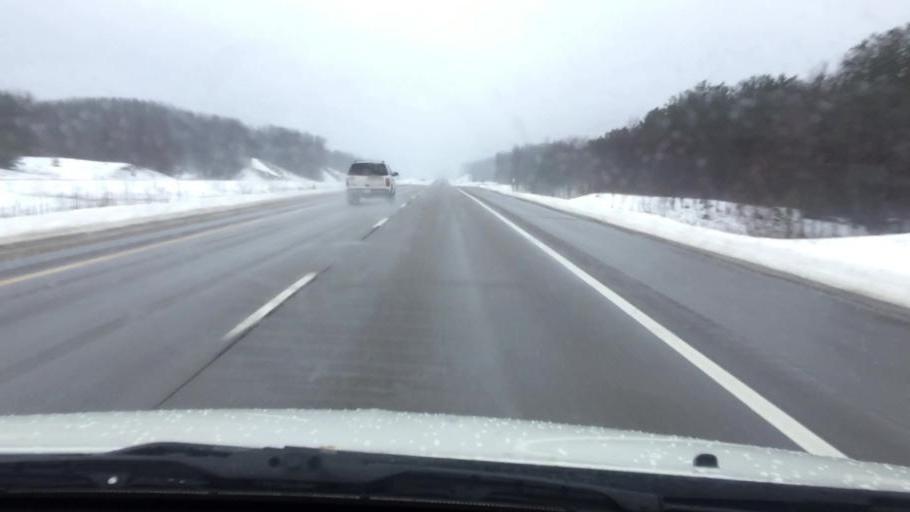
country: US
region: Michigan
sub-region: Wexford County
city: Manton
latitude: 44.3627
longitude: -85.4028
